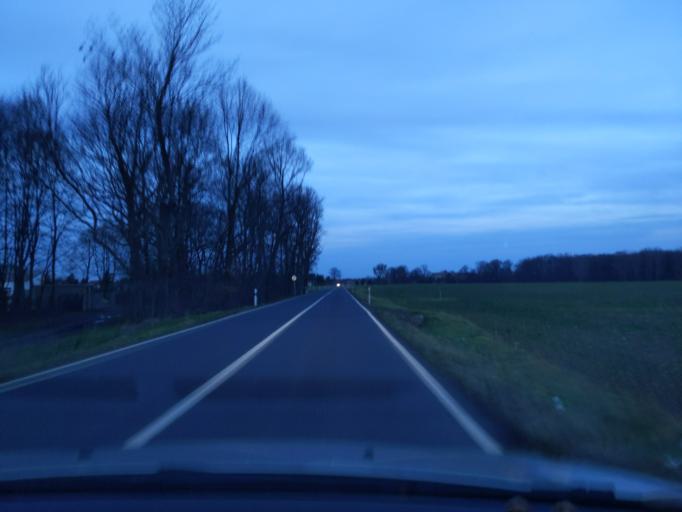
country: DE
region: Saxony
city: Guttau
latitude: 51.2532
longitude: 14.5493
